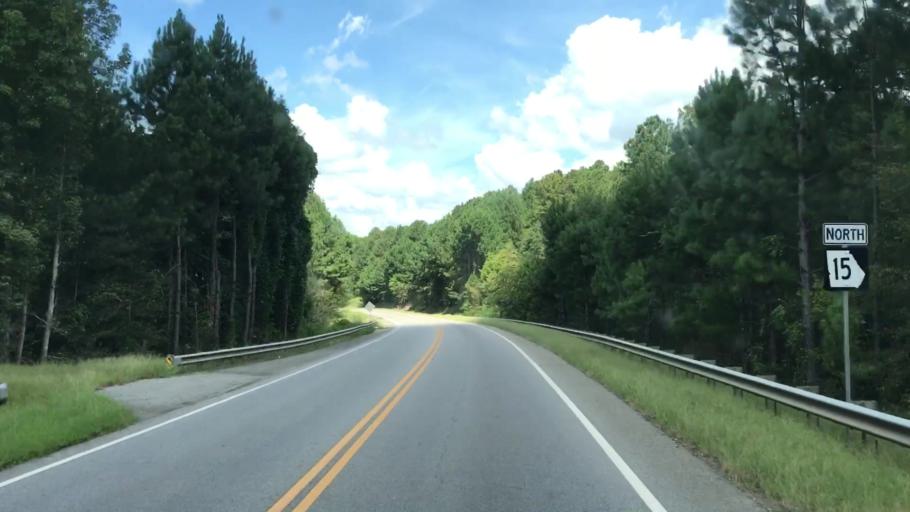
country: US
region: Georgia
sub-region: Greene County
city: Greensboro
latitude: 33.7149
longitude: -83.2919
